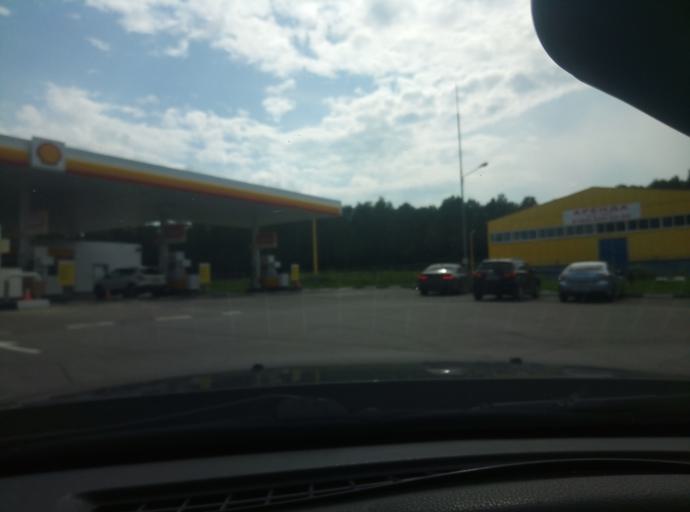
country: RU
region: Tula
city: Barsuki
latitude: 54.3393
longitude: 37.5464
